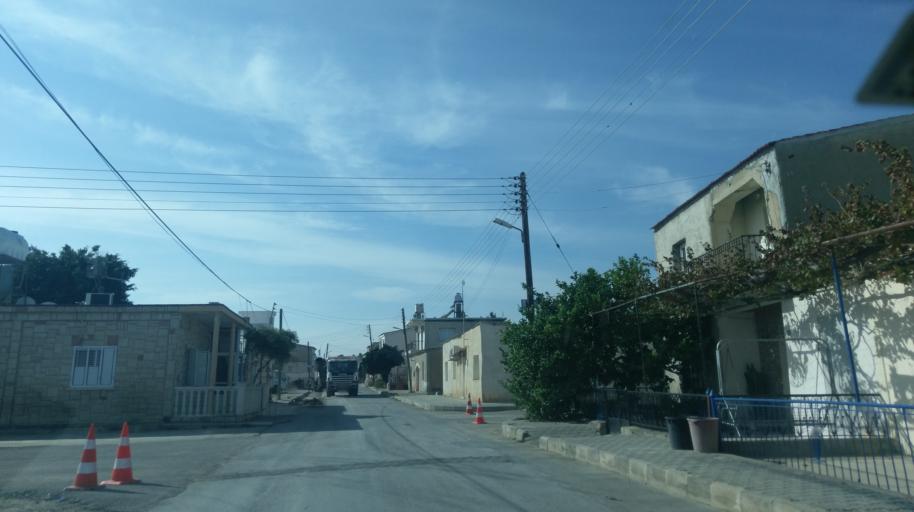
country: CY
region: Larnaka
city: Pergamos
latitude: 35.1364
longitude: 33.6588
